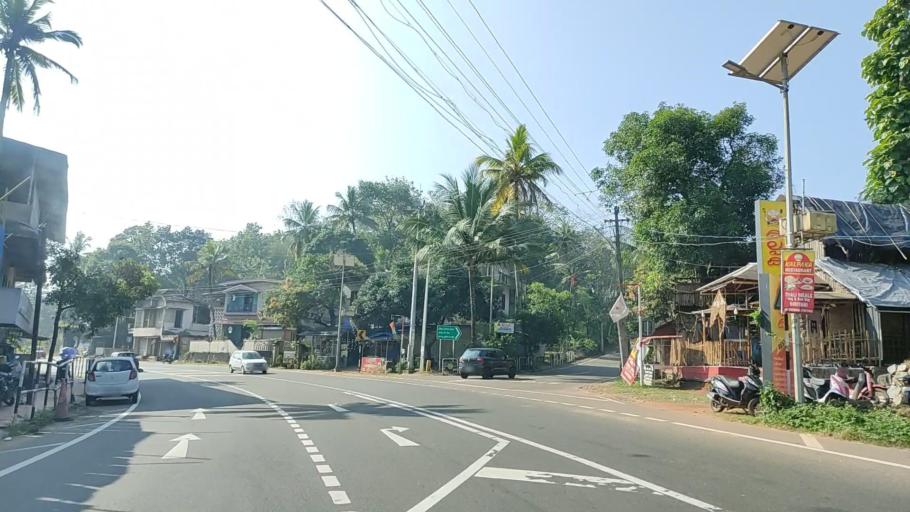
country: IN
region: Kerala
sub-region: Kollam
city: Punalur
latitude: 8.8648
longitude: 76.8708
